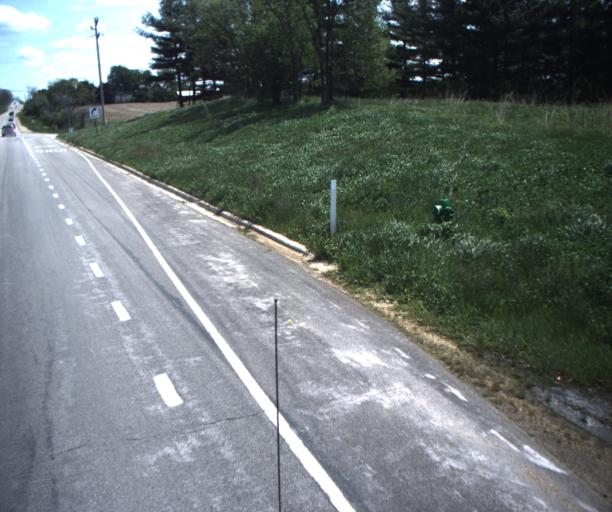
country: US
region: Illinois
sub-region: Kane County
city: Batavia
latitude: 41.8649
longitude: -88.3654
